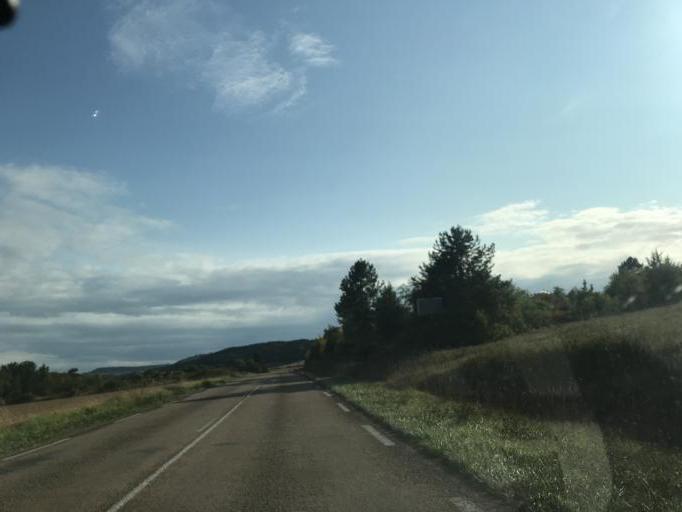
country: FR
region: Bourgogne
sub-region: Departement de l'Yonne
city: Avallon
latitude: 47.5102
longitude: 3.7649
